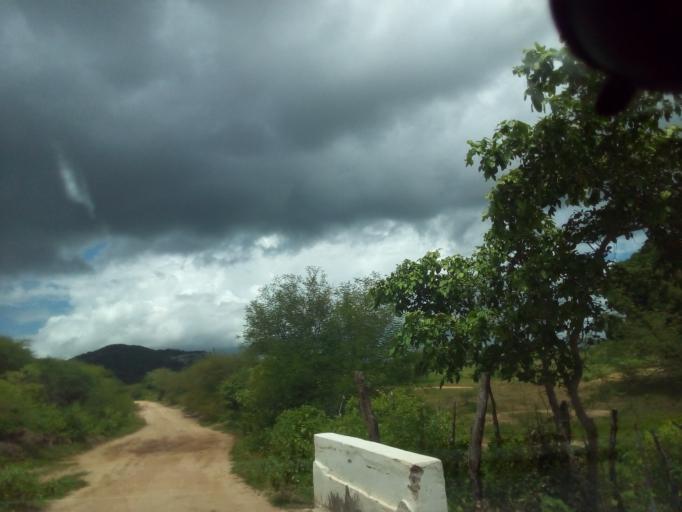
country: BR
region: Rio Grande do Norte
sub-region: Sao Tome
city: Sao Tome
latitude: -5.9520
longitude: -35.9179
